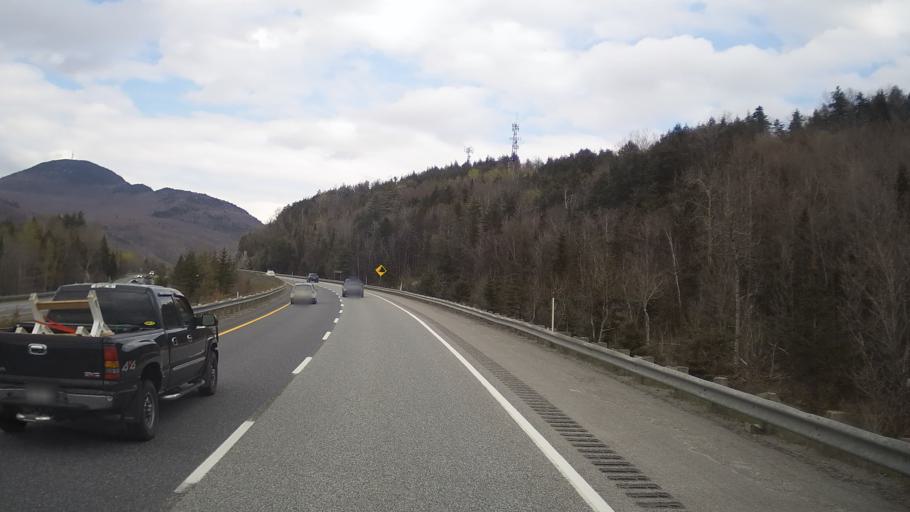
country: CA
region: Quebec
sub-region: Estrie
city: Magog
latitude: 45.2859
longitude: -72.2737
